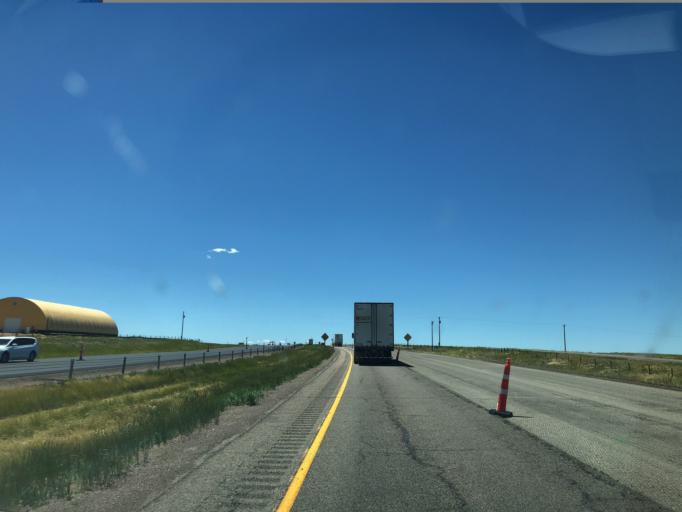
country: US
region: Wyoming
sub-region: Laramie County
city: Cheyenne
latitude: 41.0999
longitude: -105.1487
